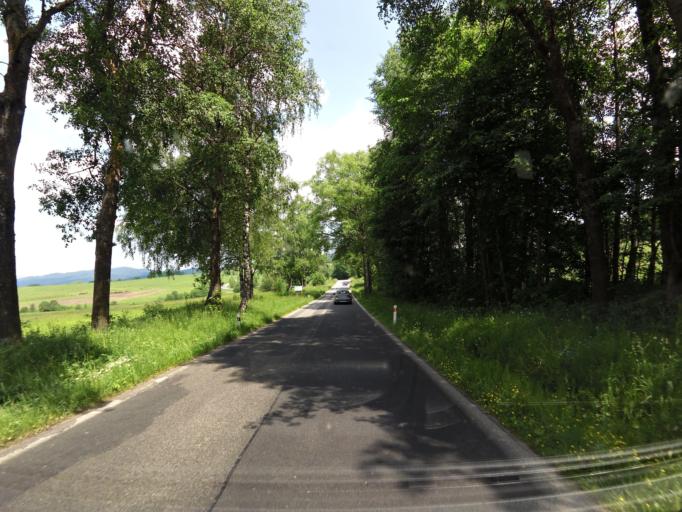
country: CZ
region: Jihocesky
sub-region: Okres Cesky Krumlov
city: Horni Plana
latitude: 48.8148
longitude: 13.9660
